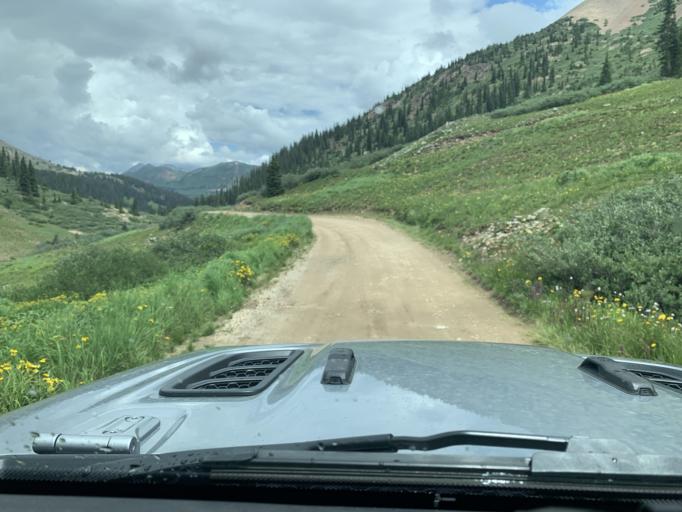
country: US
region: Colorado
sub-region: Gunnison County
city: Crested Butte
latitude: 38.9969
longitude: -107.0576
